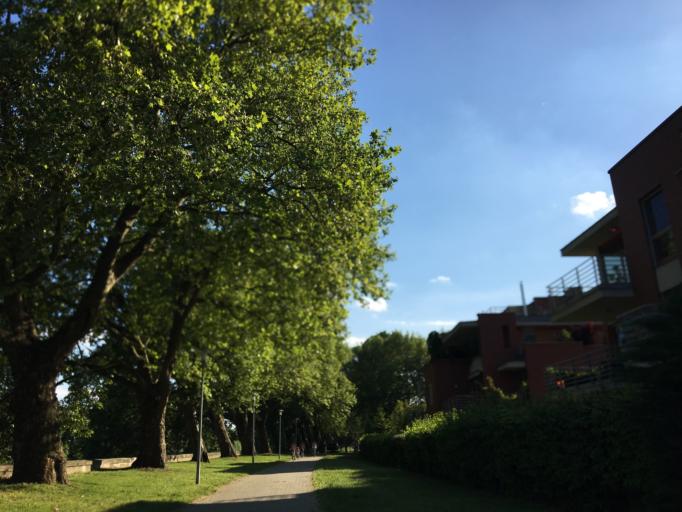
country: HU
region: Budapest
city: Budapest III. keruelet
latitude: 47.5582
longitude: 19.0541
